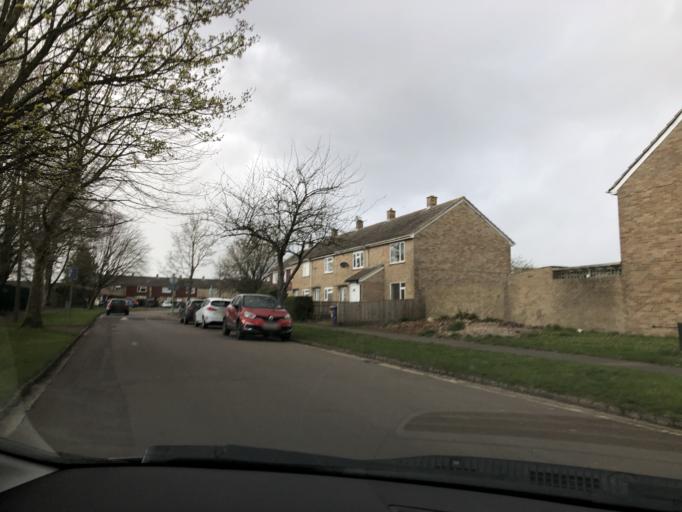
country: GB
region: England
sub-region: Oxfordshire
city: Bicester
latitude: 51.9001
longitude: -1.1662
